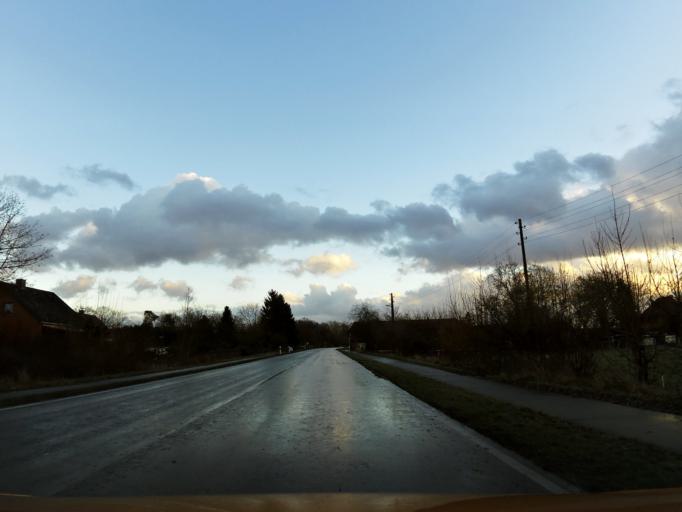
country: DE
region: Lower Saxony
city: Meinersen
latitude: 52.4539
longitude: 10.3076
